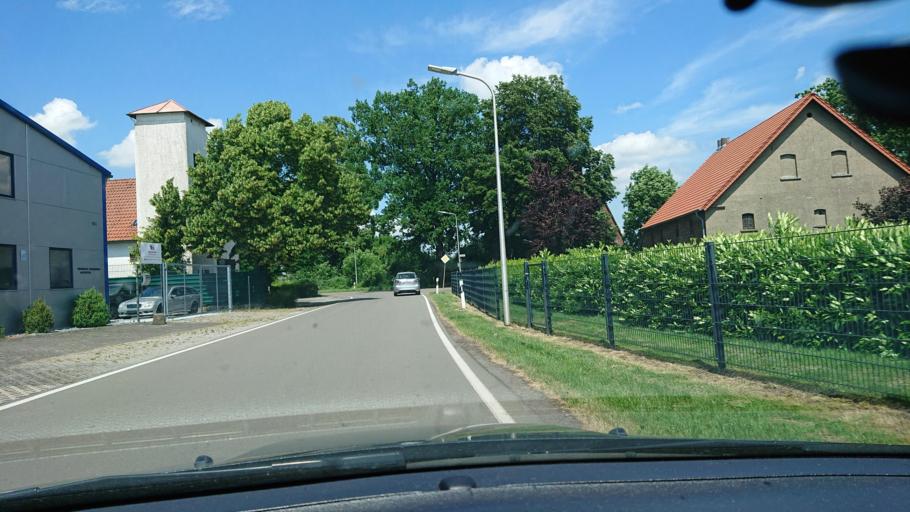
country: DE
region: North Rhine-Westphalia
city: Preussisch Oldendorf
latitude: 52.3131
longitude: 8.4848
